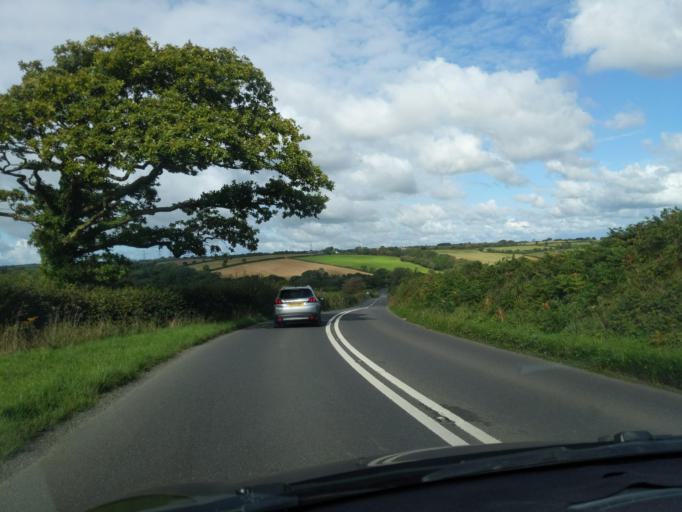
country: GB
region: England
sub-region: Devon
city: Holsworthy
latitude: 50.8647
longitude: -4.3241
